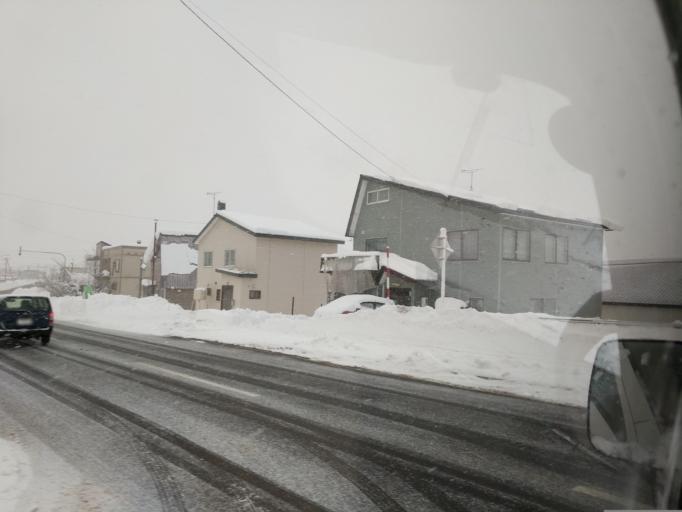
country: JP
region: Hokkaido
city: Niseko Town
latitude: 42.8898
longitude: 140.7455
